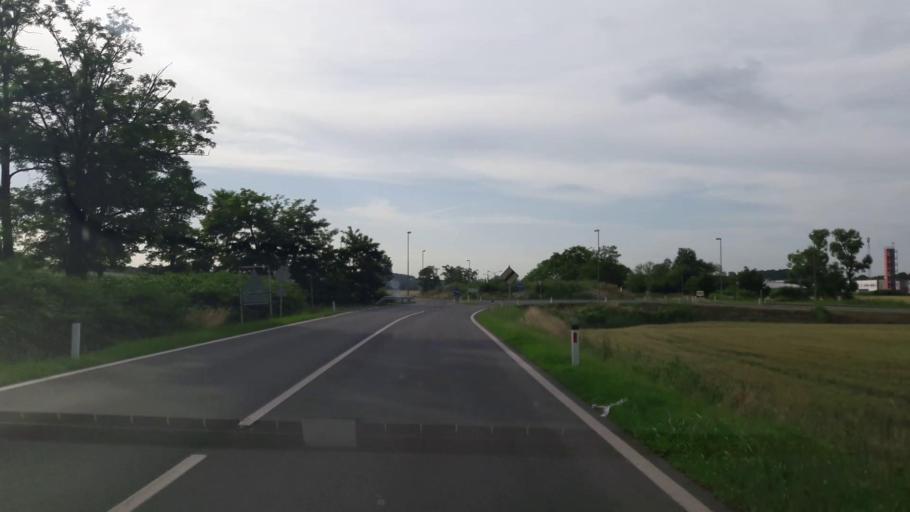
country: AT
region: Burgenland
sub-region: Politischer Bezirk Oberpullendorf
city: Oberpullendorf
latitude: 47.4831
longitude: 16.5271
